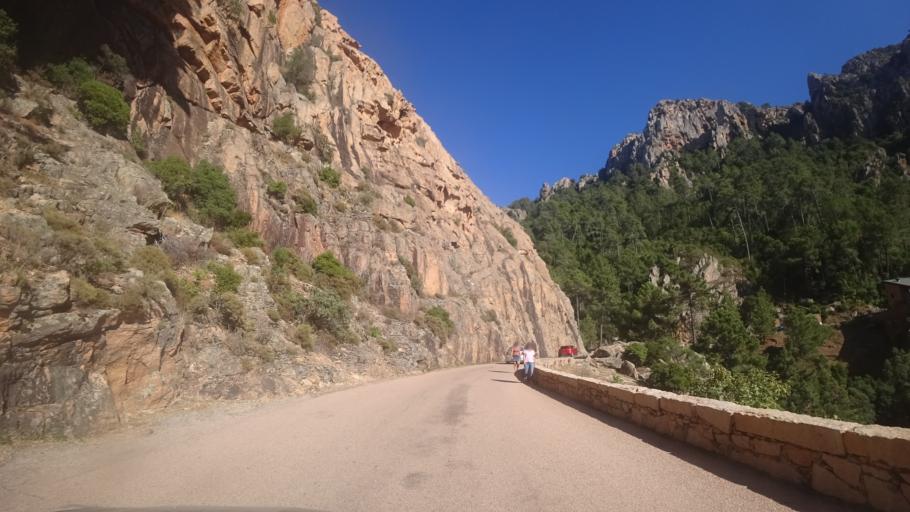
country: FR
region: Corsica
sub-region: Departement de la Corse-du-Sud
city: Cargese
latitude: 42.2496
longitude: 8.6601
